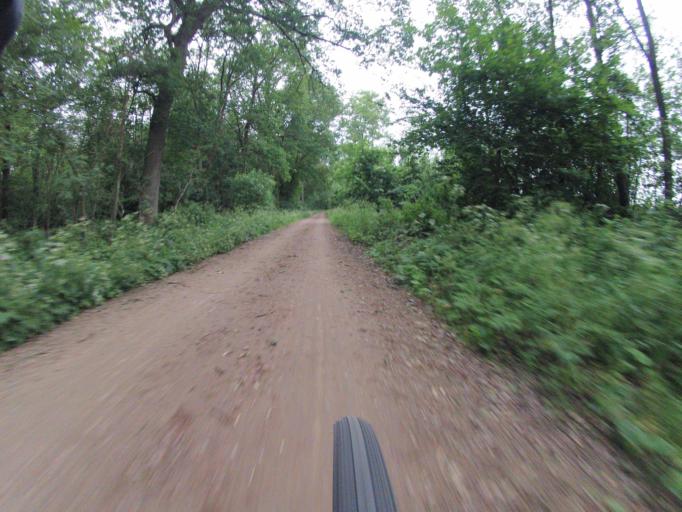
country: DE
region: North Rhine-Westphalia
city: Emsdetten
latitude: 52.2177
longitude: 7.5531
